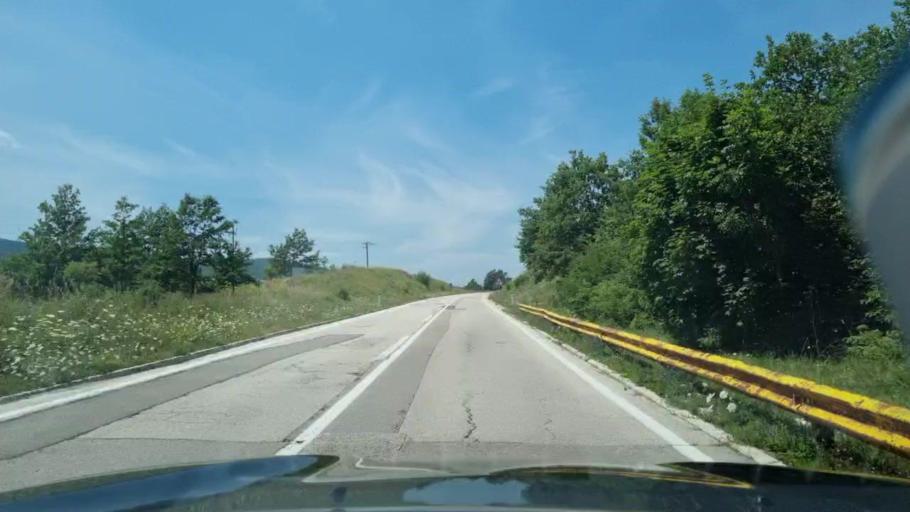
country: BA
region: Federation of Bosnia and Herzegovina
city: Sanica
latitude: 44.5524
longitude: 16.5561
